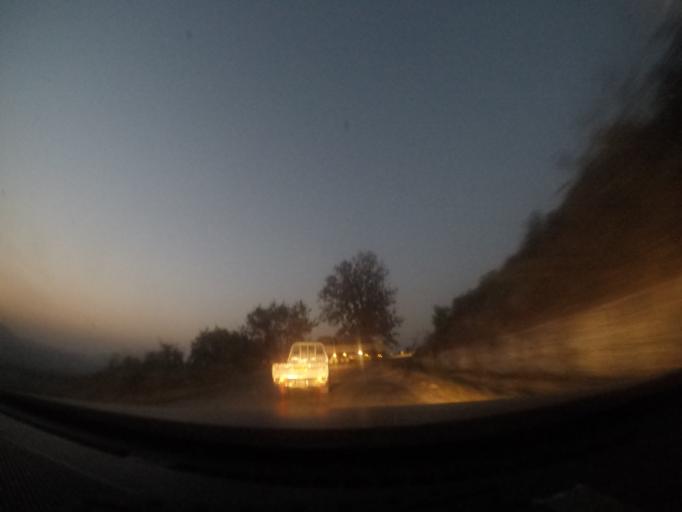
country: MM
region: Mandalay
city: Yamethin
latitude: 20.7108
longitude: 96.5154
